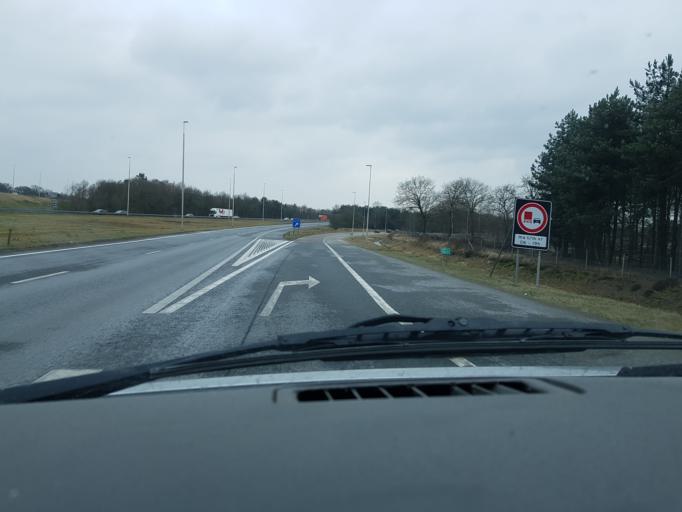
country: NL
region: North Brabant
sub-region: Gemeente Oss
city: Berghem
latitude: 51.7381
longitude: 5.5786
